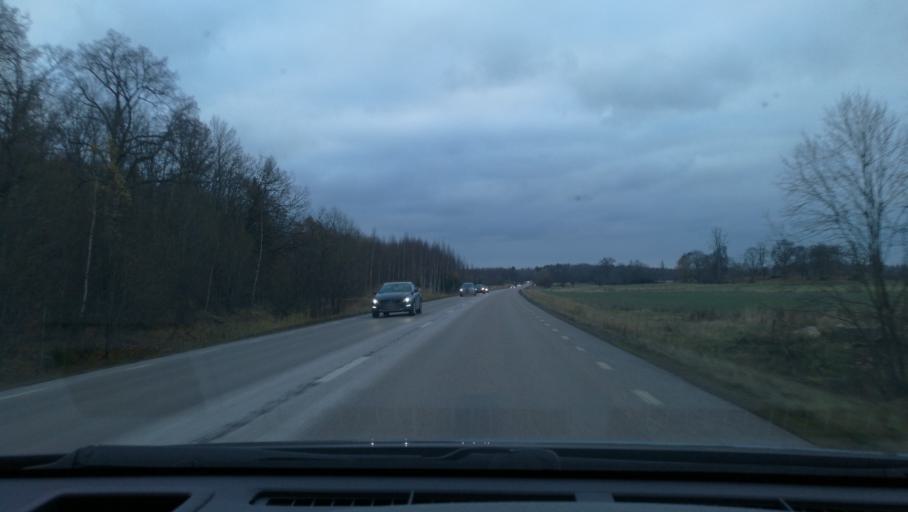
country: SE
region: Soedermanland
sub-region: Eskilstuna Kommun
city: Kvicksund
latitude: 59.4881
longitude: 16.3055
